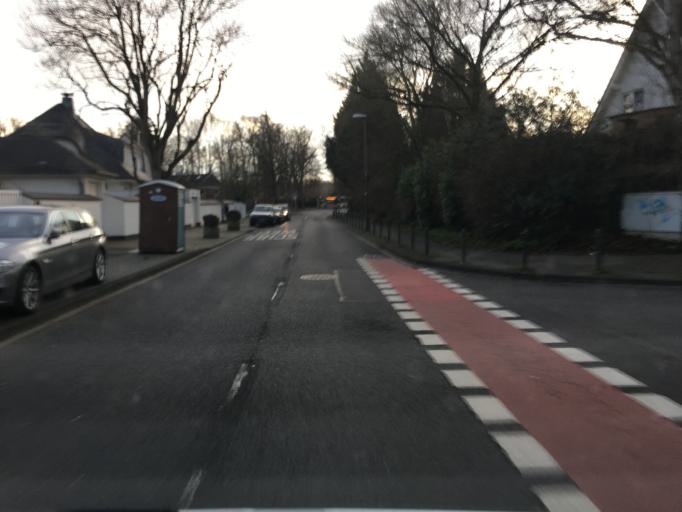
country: DE
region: North Rhine-Westphalia
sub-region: Regierungsbezirk Koln
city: Neustadt/Sued
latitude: 50.9181
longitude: 6.9000
